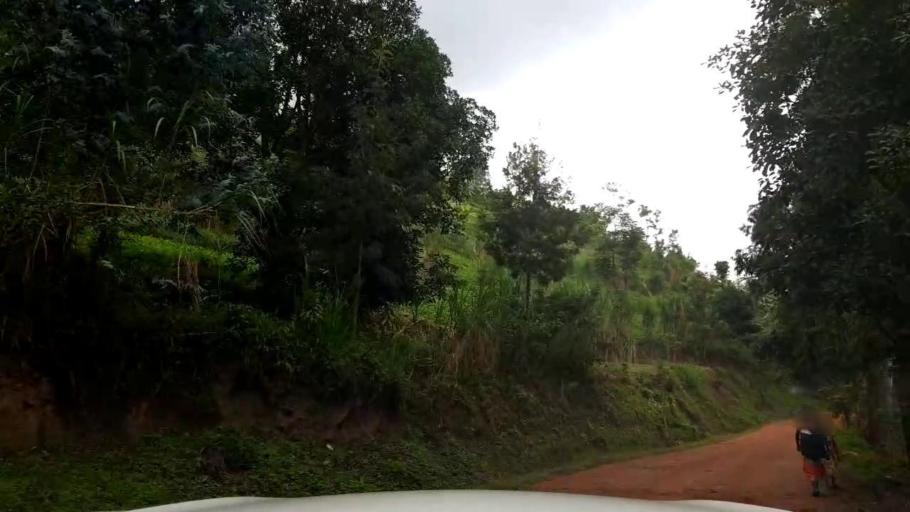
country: UG
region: Western Region
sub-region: Kisoro District
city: Kisoro
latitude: -1.3928
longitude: 29.7992
